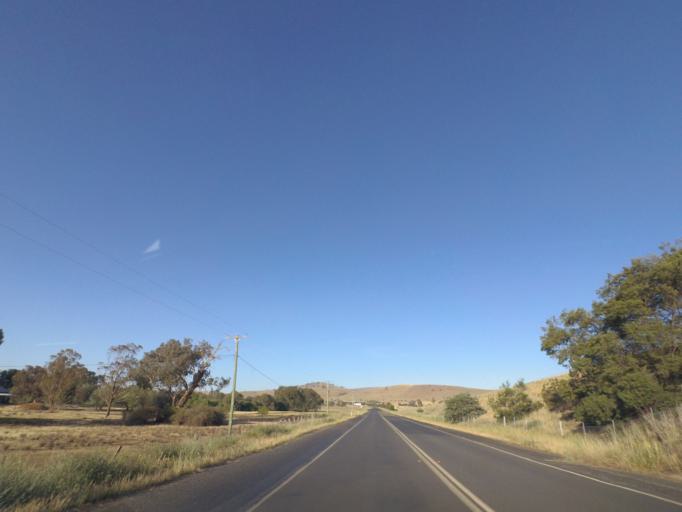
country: AU
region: New South Wales
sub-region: Gundagai
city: Gundagai
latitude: -34.9542
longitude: 148.1594
